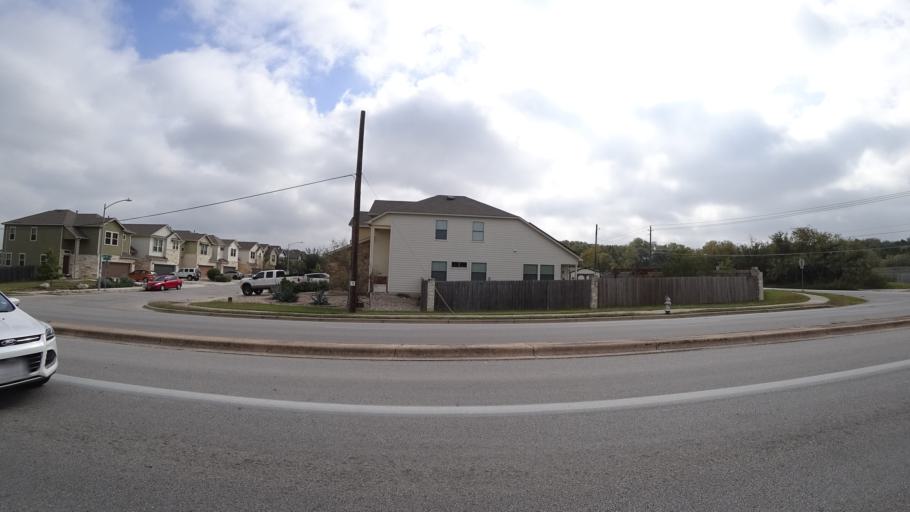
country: US
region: Texas
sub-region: Travis County
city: Shady Hollow
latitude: 30.1950
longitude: -97.8308
